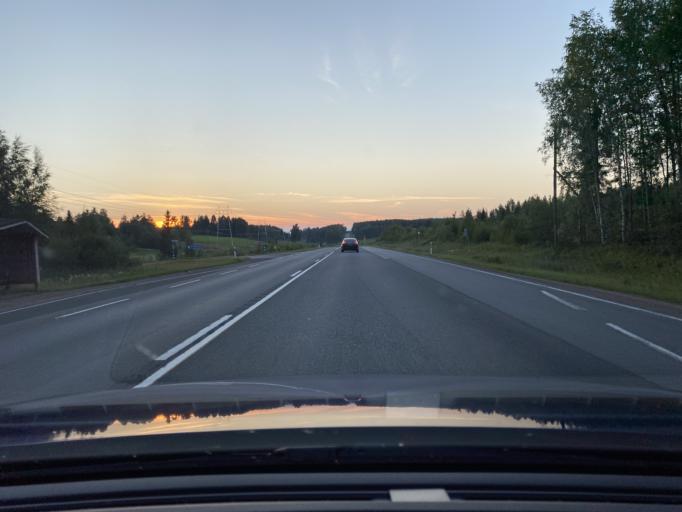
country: FI
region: Pirkanmaa
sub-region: Luoteis-Pirkanmaa
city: Ikaalinen
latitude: 61.8095
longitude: 22.9617
